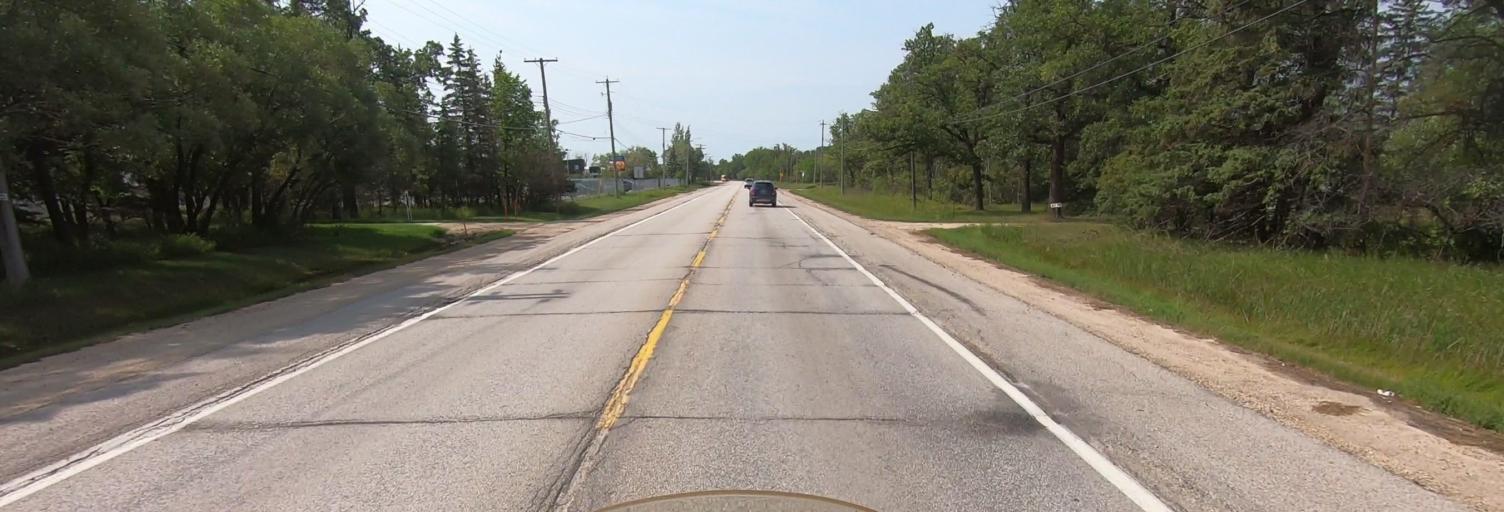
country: CA
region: Manitoba
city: Winnipeg
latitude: 49.7844
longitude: -97.1219
